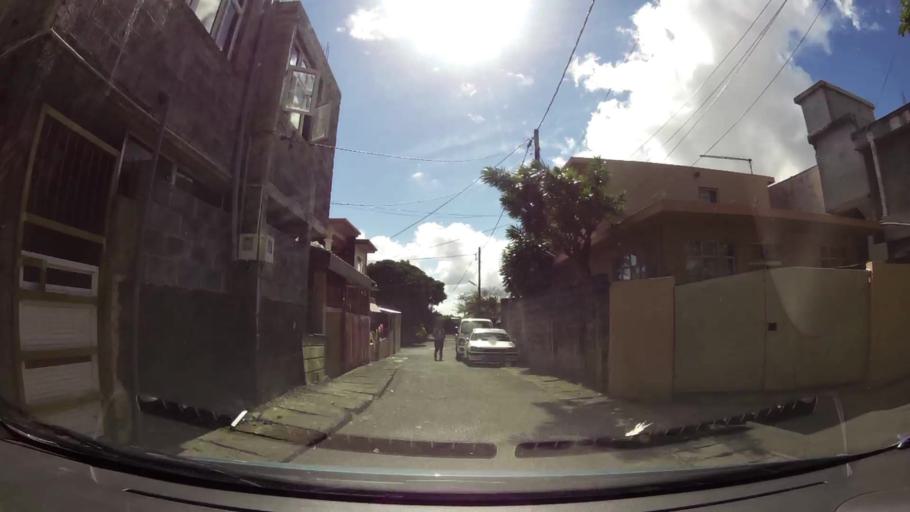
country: MU
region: Plaines Wilhems
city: Curepipe
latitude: -20.3293
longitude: 57.5217
